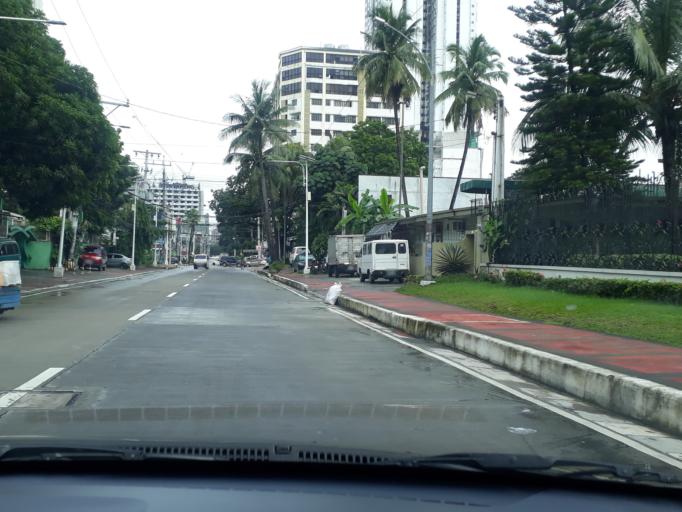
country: PH
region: Metro Manila
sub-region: Quezon City
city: Quezon City
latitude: 14.6352
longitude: 121.0389
